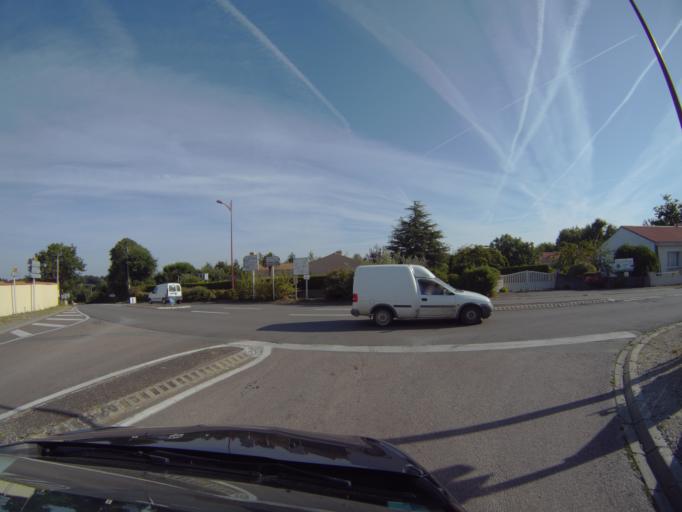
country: FR
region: Pays de la Loire
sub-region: Departement de la Vendee
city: Nieul-le-Dolent
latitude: 46.5774
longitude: -1.5112
